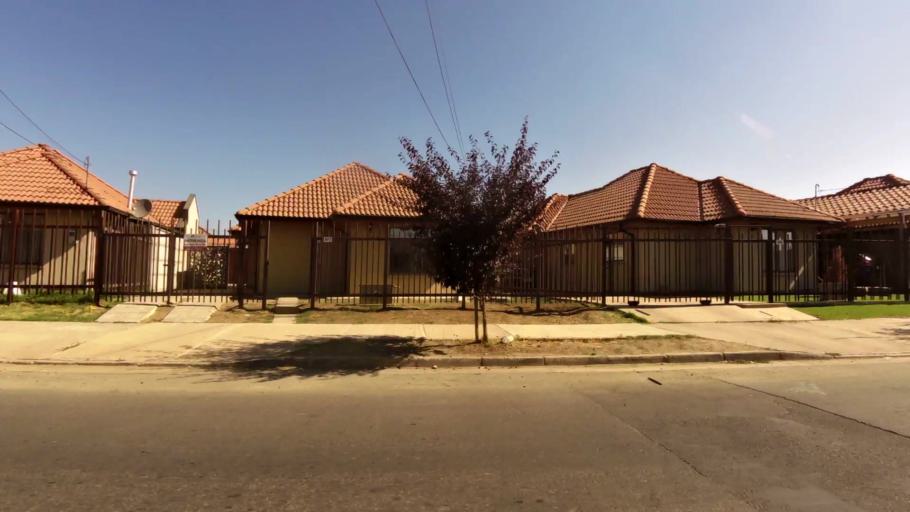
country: CL
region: Maule
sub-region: Provincia de Talca
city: Talca
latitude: -35.4208
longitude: -71.6117
